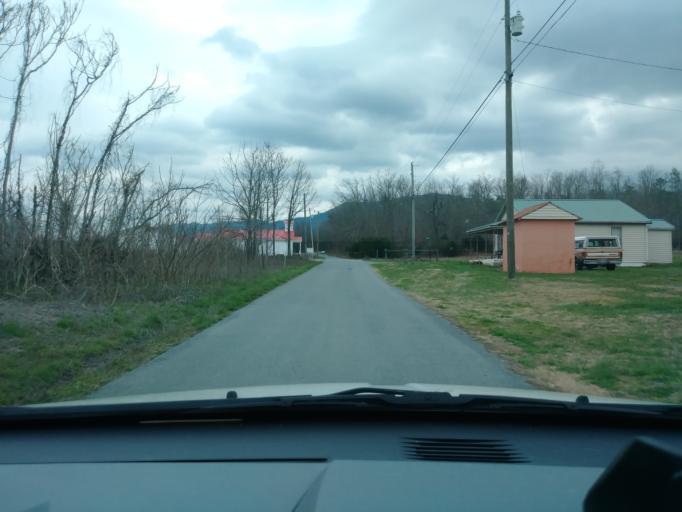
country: US
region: Tennessee
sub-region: Greene County
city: Tusculum
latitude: 36.0860
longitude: -82.7371
